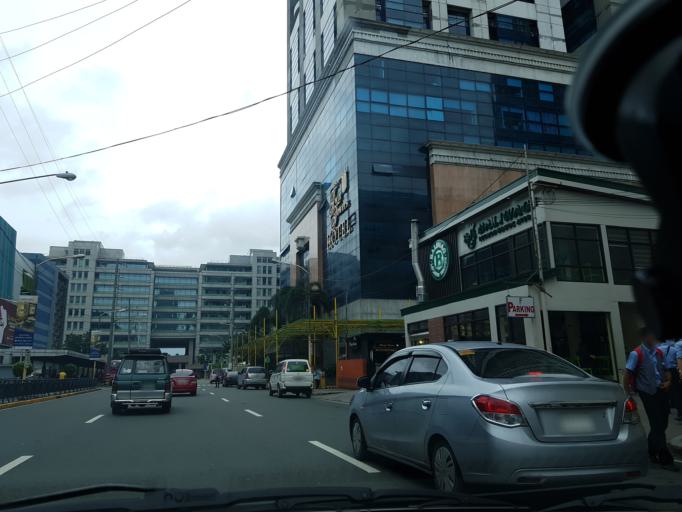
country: PH
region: Metro Manila
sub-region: Pasig
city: Pasig City
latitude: 14.5855
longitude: 121.0579
